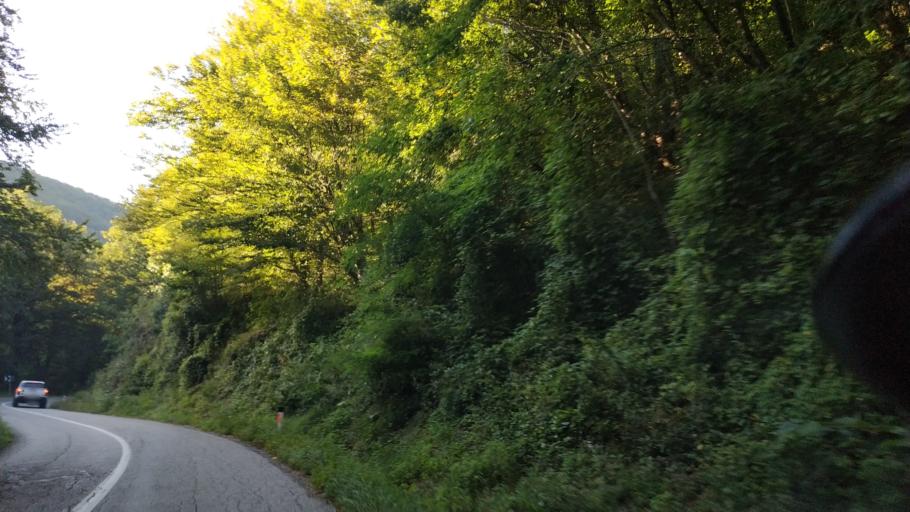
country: RS
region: Central Serbia
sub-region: Rasinski Okrug
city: Krusevac
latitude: 43.4532
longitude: 21.3589
